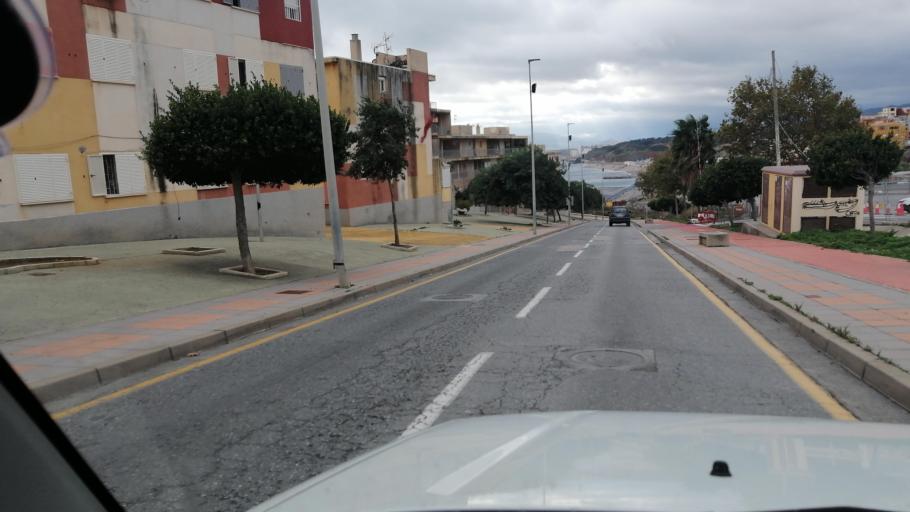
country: ES
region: Ceuta
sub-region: Ceuta
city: Ceuta
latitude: 35.8794
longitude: -5.3398
